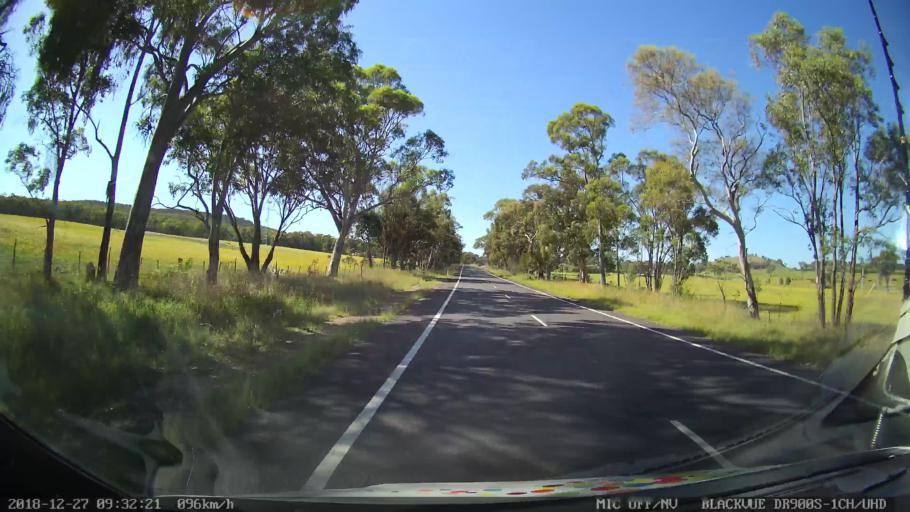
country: AU
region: New South Wales
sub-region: Lithgow
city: Portland
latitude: -33.2060
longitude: 150.0154
